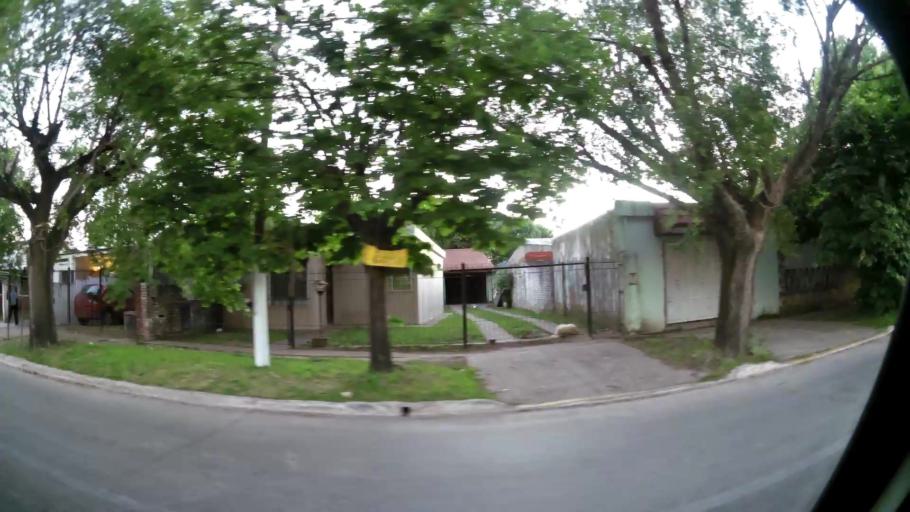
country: AR
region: Buenos Aires
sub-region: Partido de Quilmes
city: Quilmes
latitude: -34.8034
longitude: -58.1820
